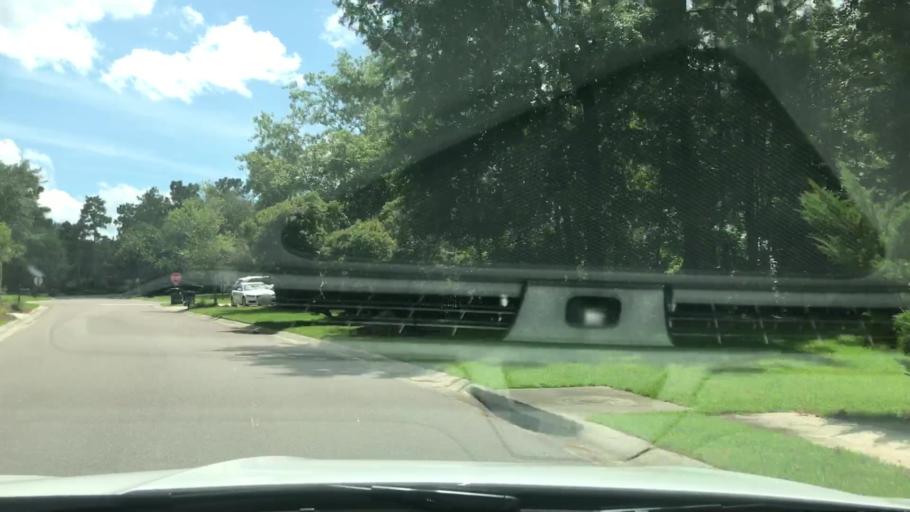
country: US
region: South Carolina
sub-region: Dorchester County
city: Summerville
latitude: 33.0364
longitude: -80.2256
